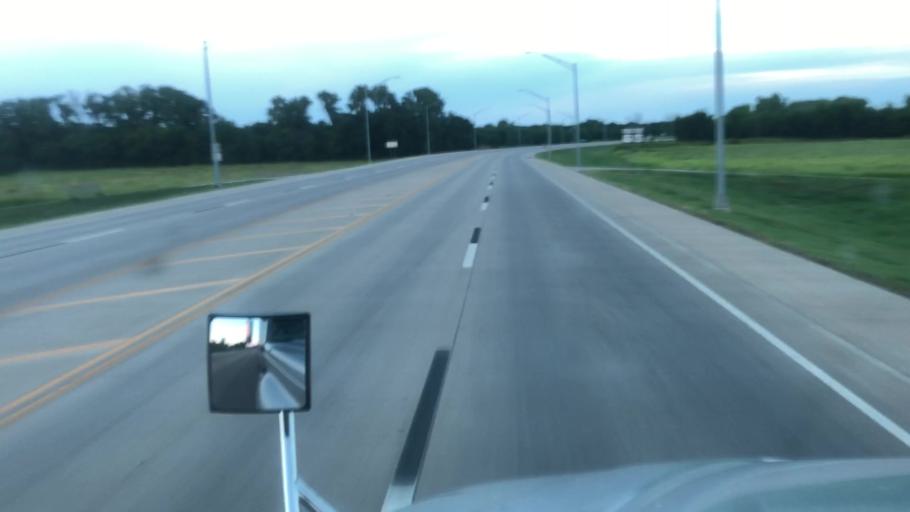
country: US
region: Oklahoma
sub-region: Kay County
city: Ponca City
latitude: 36.6820
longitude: -97.0700
